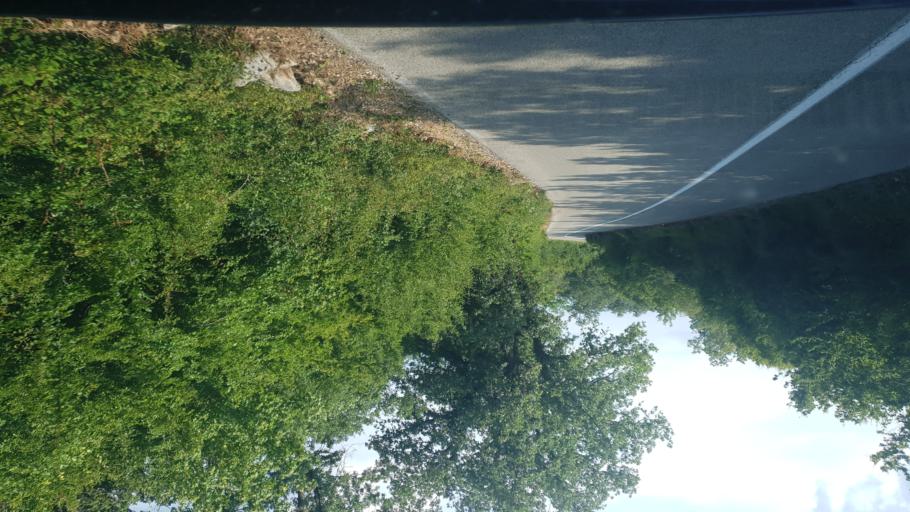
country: HR
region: Primorsko-Goranska
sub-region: Grad Crikvenica
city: Crikvenica
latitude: 45.1122
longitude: 14.6329
